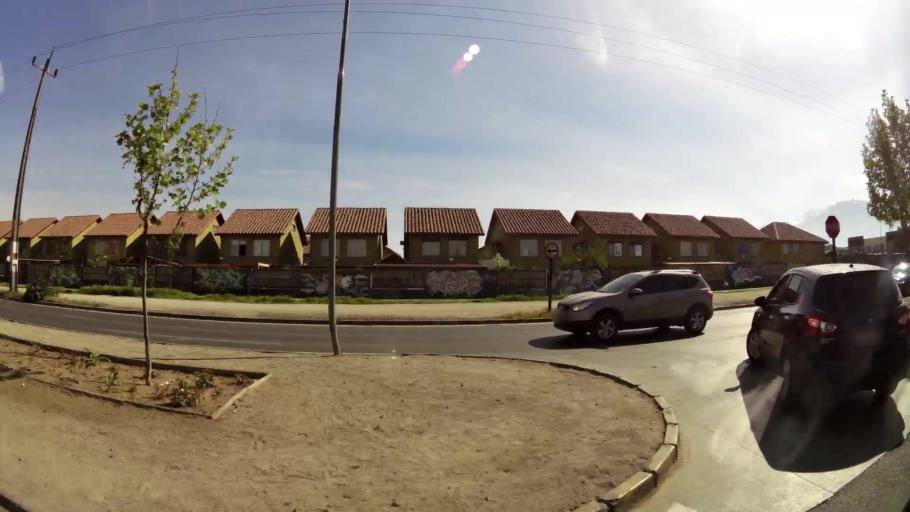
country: CL
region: Santiago Metropolitan
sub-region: Provincia de Cordillera
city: Puente Alto
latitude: -33.6034
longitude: -70.5805
